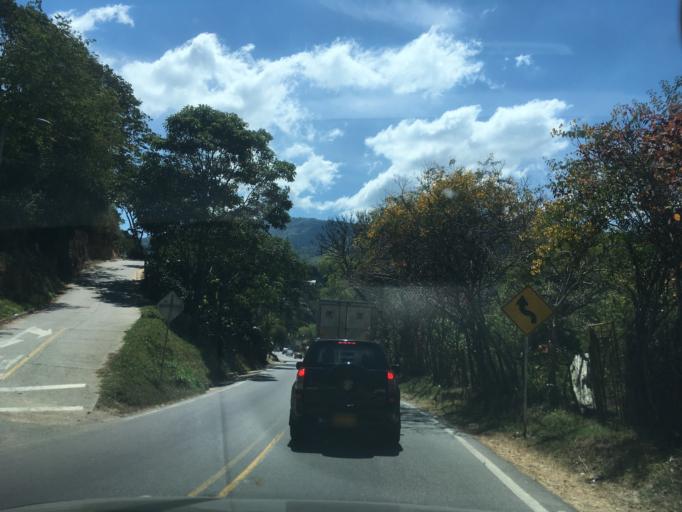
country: CO
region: Santander
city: Aratoca
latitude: 6.7013
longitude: -73.0149
